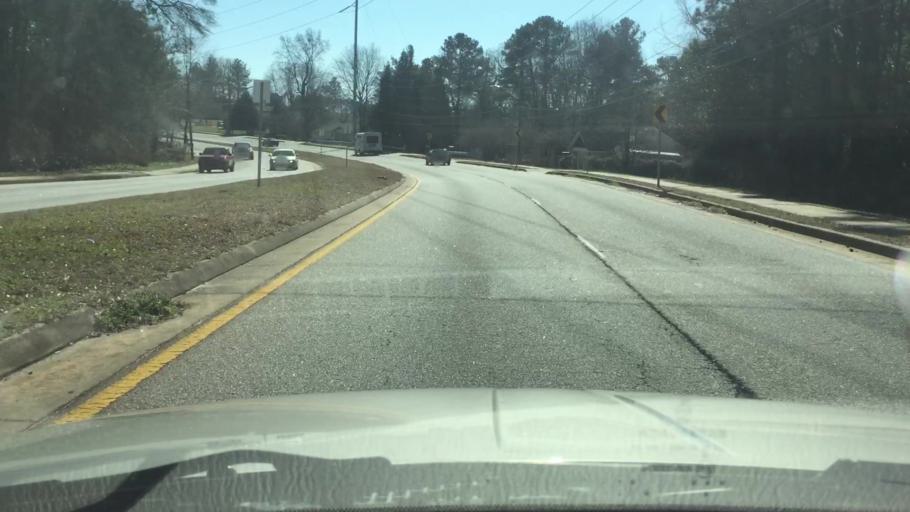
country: US
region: Georgia
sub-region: DeKalb County
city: Redan
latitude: 33.7428
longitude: -84.1962
